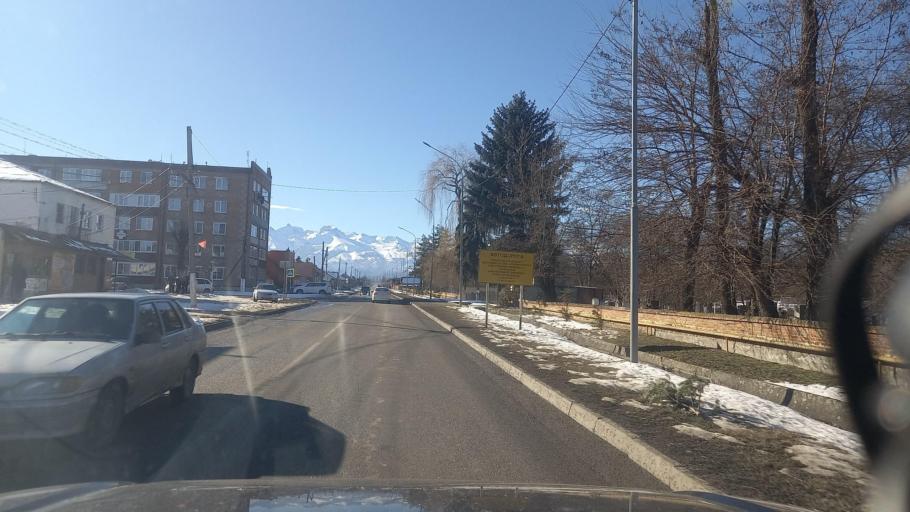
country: RU
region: North Ossetia
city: Chikola
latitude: 43.1982
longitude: 43.9215
